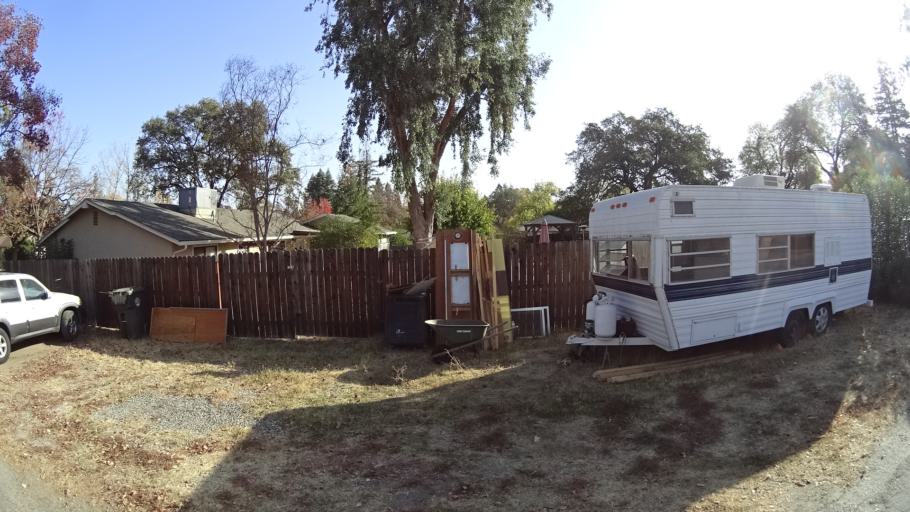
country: US
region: California
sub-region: Sacramento County
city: Citrus Heights
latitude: 38.6981
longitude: -121.2591
